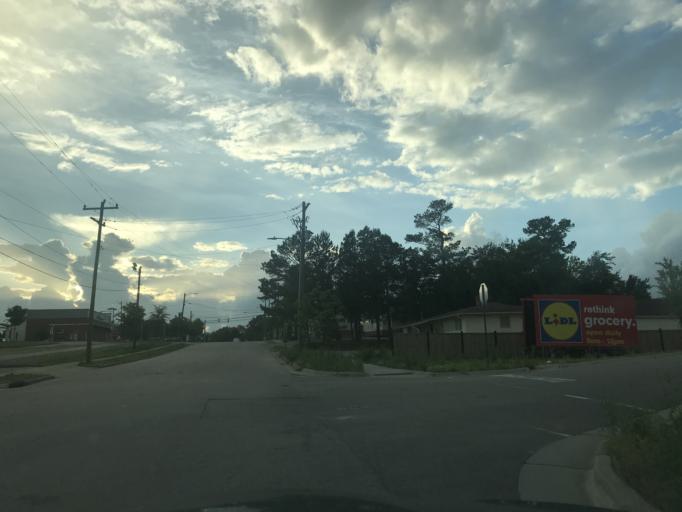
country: US
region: North Carolina
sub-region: Wake County
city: Raleigh
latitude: 35.8385
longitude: -78.6101
